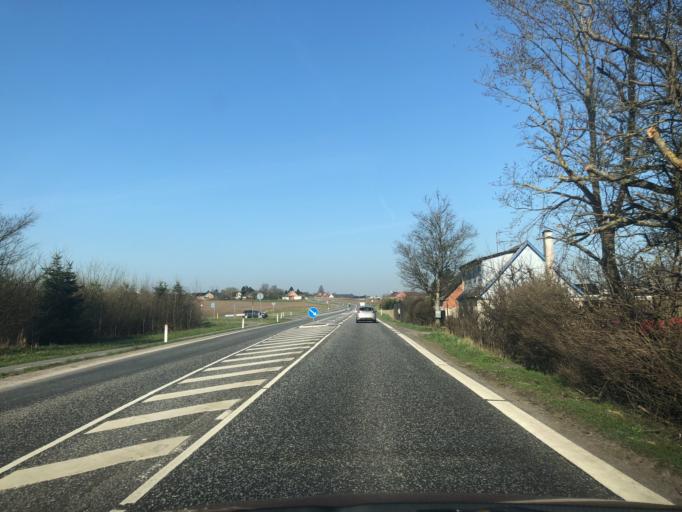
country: DK
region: Zealand
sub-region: Faxe Kommune
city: Ronnede
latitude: 55.2581
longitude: 12.0401
